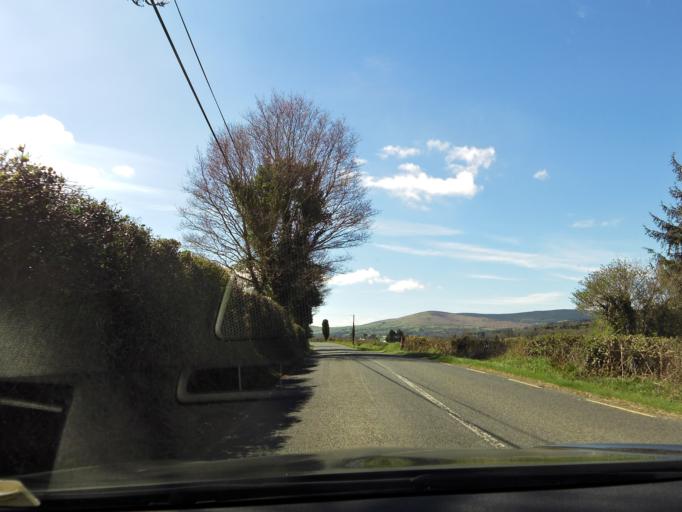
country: IE
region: Leinster
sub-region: Wicklow
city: Aughrim
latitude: 52.8240
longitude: -6.3731
